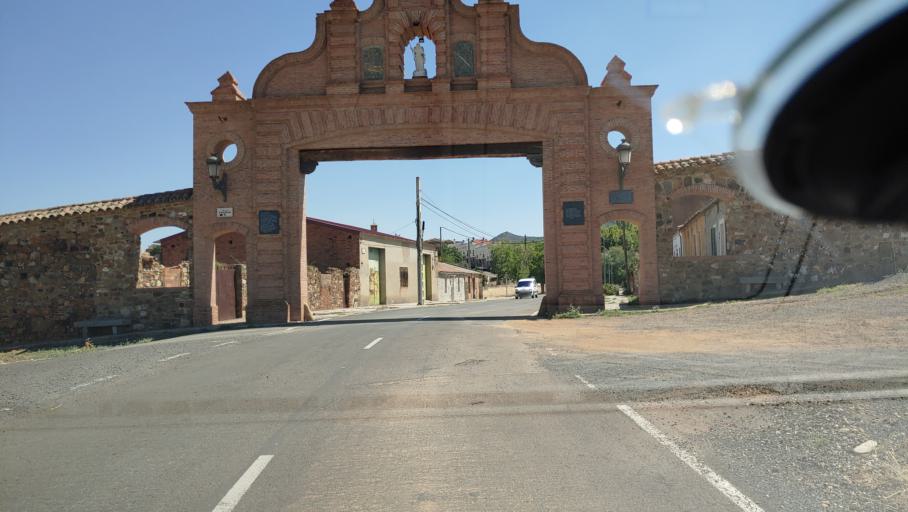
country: ES
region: Castille-La Mancha
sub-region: Provincia de Ciudad Real
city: Alamillo
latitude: 38.7402
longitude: -4.7170
